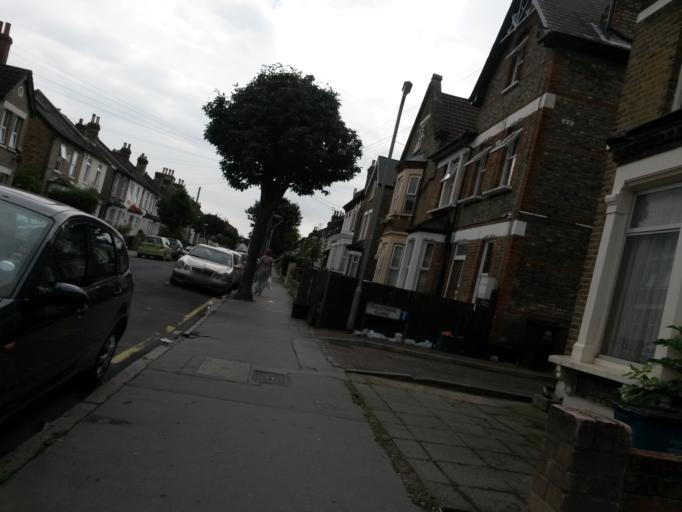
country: GB
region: England
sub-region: Greater London
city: Croydon
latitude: 51.3866
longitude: -0.0956
